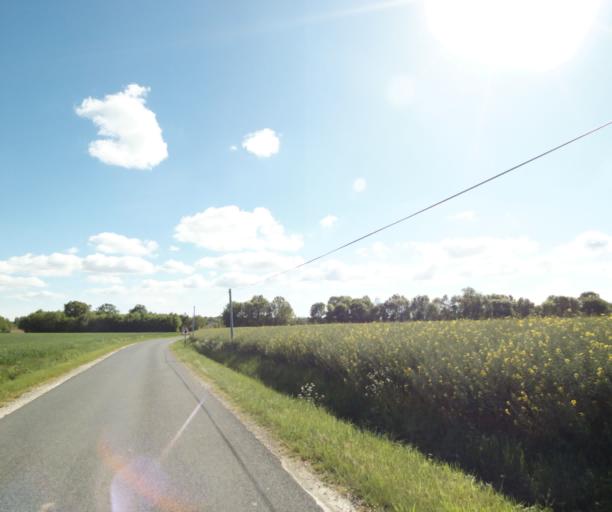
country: FR
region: Poitou-Charentes
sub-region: Departement de la Charente-Maritime
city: Saint-Georges-des-Coteaux
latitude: 45.7878
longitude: -0.6957
